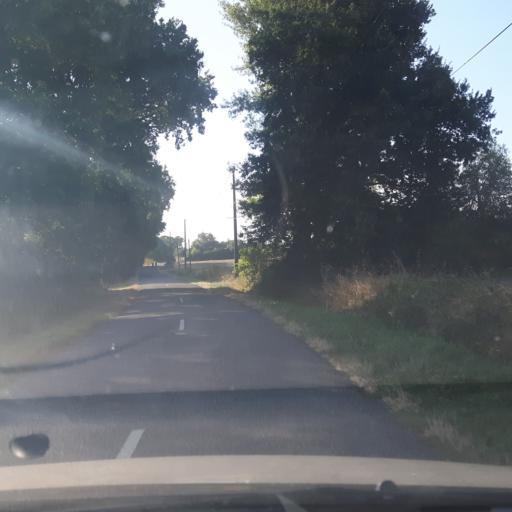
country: FR
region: Midi-Pyrenees
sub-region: Departement de la Haute-Garonne
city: Vacquiers
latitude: 43.7656
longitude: 1.4935
